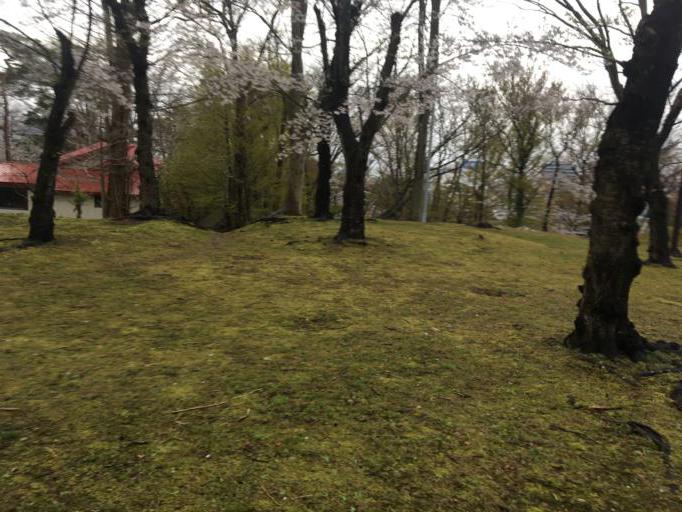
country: JP
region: Akita
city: Akita
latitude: 39.7216
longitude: 140.1228
